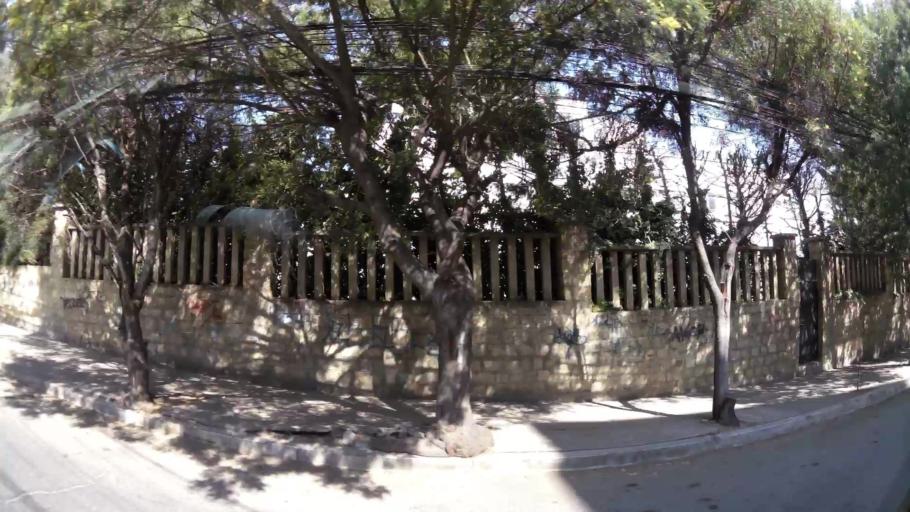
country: BO
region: La Paz
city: La Paz
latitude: -16.5407
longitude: -68.0863
